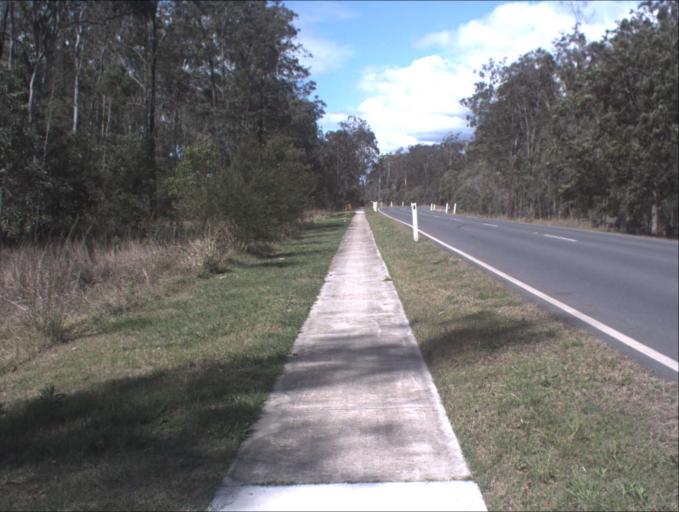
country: AU
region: Queensland
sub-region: Logan
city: Park Ridge South
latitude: -27.7434
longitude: 153.0506
